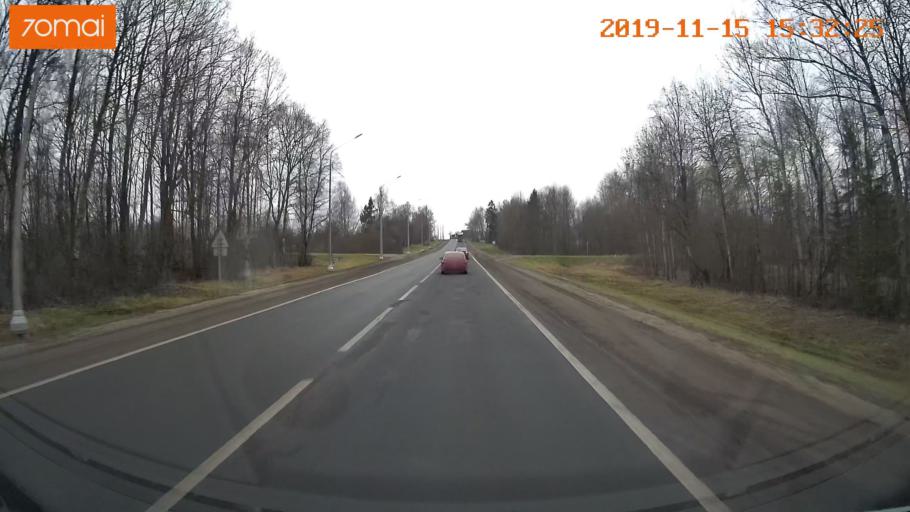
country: RU
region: Jaroslavl
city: Danilov
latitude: 58.0904
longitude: 40.1004
